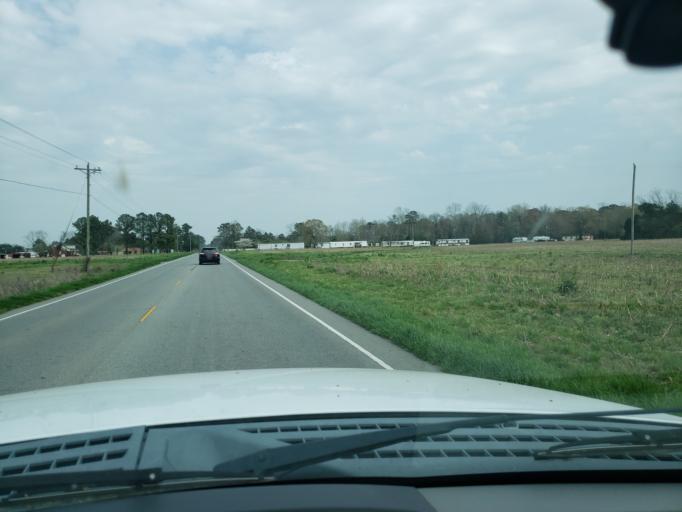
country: US
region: North Carolina
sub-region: Duplin County
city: Wallace
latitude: 34.7865
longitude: -77.8970
